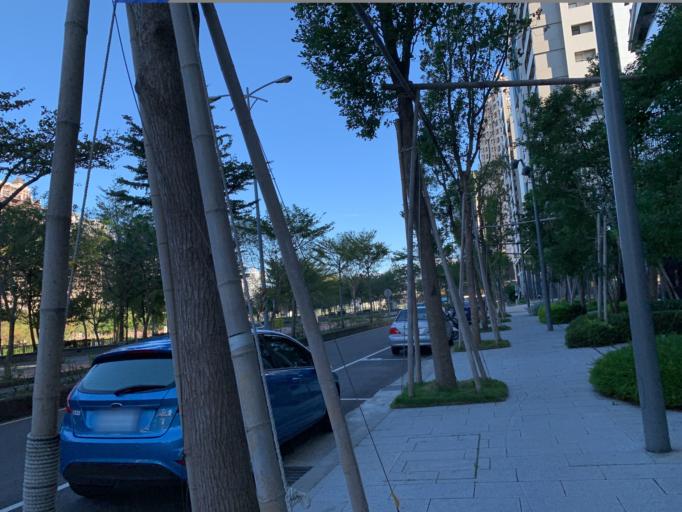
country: TW
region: Taiwan
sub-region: Hsinchu
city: Zhubei
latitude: 24.8096
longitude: 121.0342
